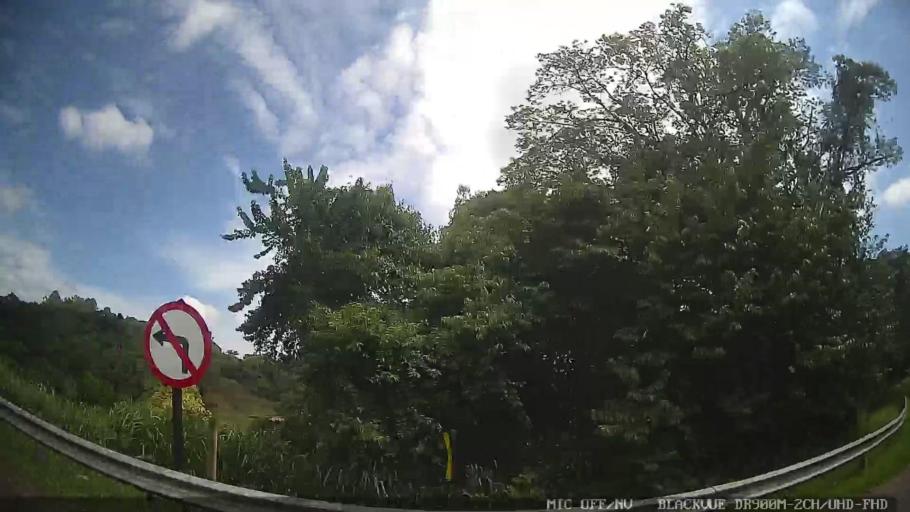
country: BR
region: Sao Paulo
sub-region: Tiete
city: Tiete
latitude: -23.1075
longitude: -47.7576
